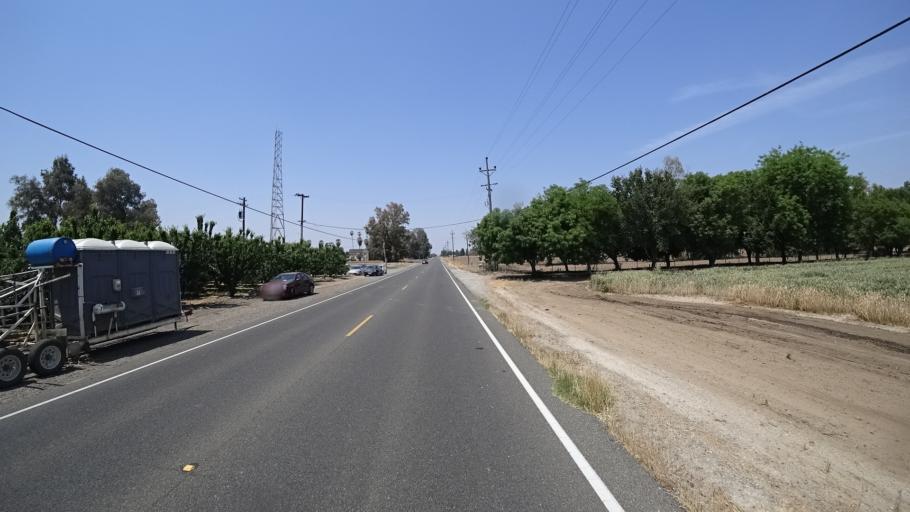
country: US
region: California
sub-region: Kings County
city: Armona
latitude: 36.3136
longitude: -119.7372
